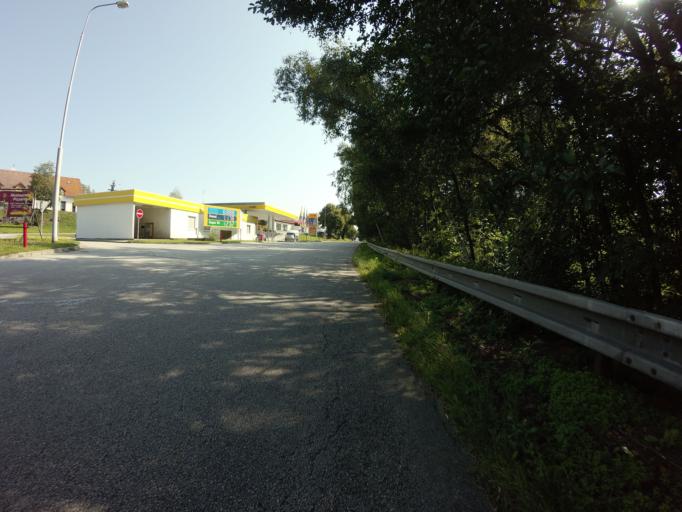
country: CZ
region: Jihocesky
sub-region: Okres Cesky Krumlov
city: Vyssi Brod
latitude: 48.5869
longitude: 14.3220
